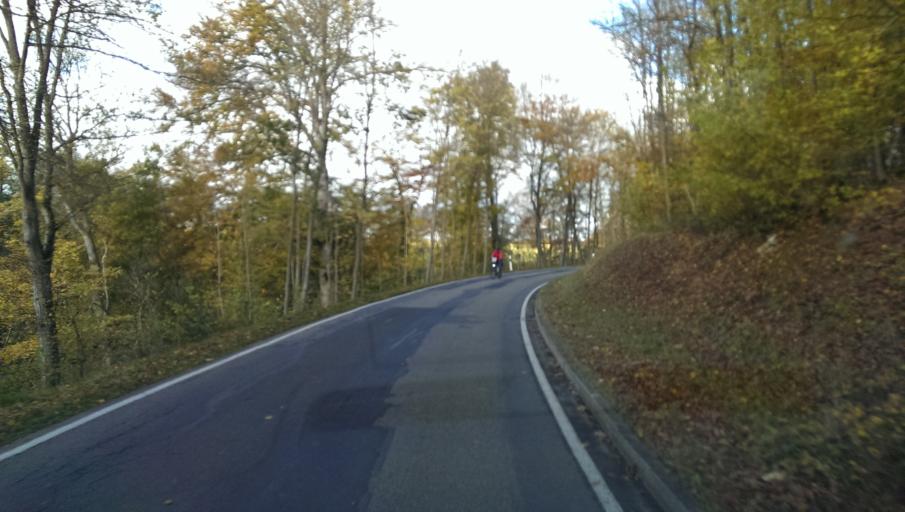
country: DE
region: Baden-Wuerttemberg
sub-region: Karlsruhe Region
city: Seckach
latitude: 49.4607
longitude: 9.3345
